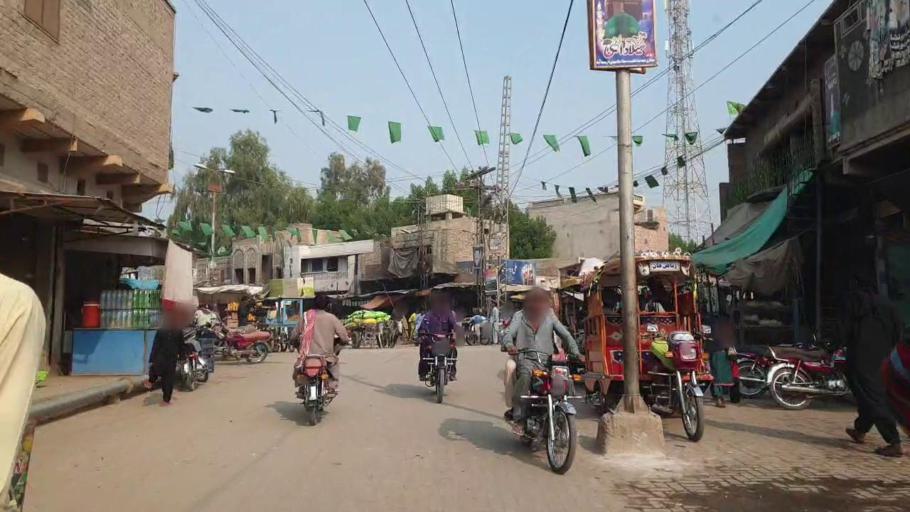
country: PK
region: Sindh
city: Bhan
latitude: 26.5557
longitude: 67.7204
